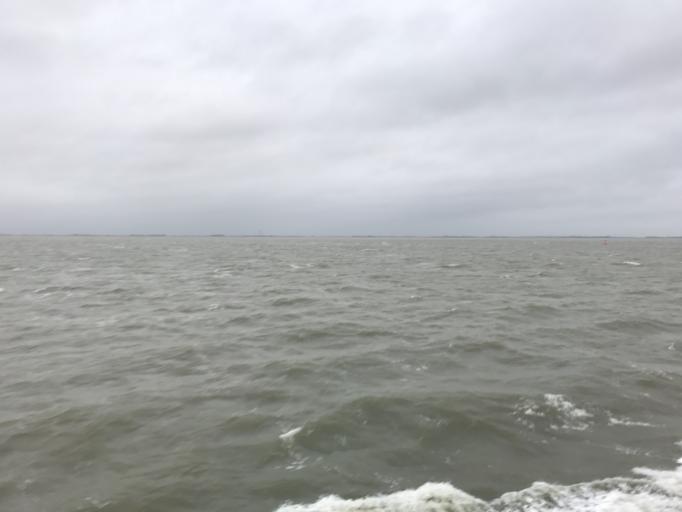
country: NL
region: Groningen
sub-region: Gemeente Delfzijl
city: Delfzijl
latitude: 53.4092
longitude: 6.9424
